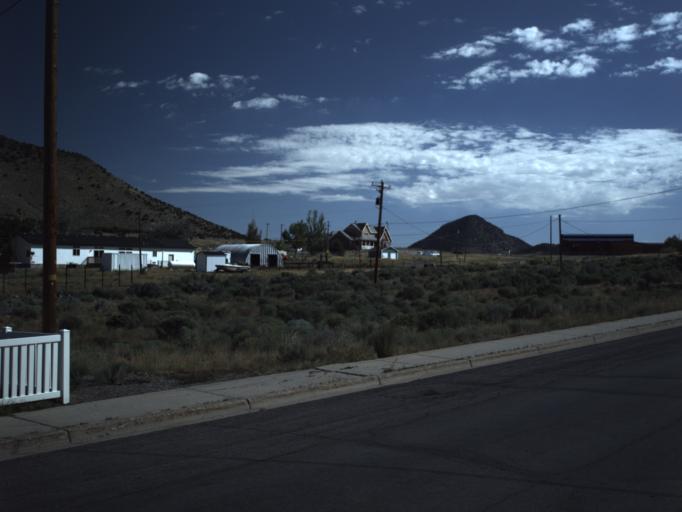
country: US
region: Utah
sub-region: Utah County
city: Genola
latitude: 39.9564
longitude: -112.1091
